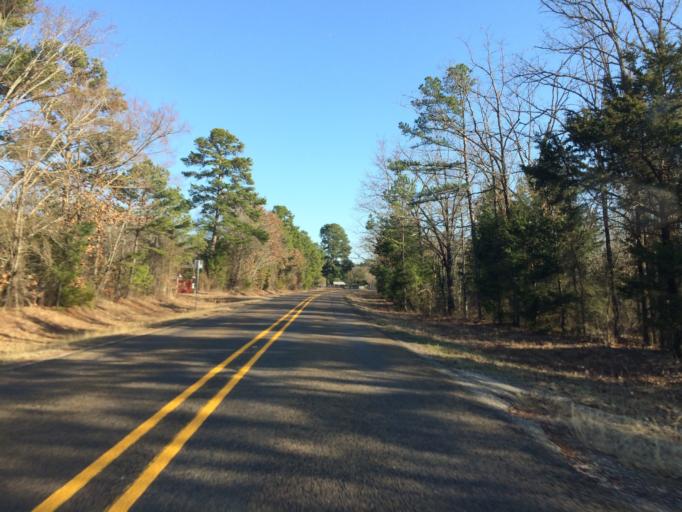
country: US
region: Texas
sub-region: Wood County
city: Mineola
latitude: 32.6885
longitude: -95.3423
